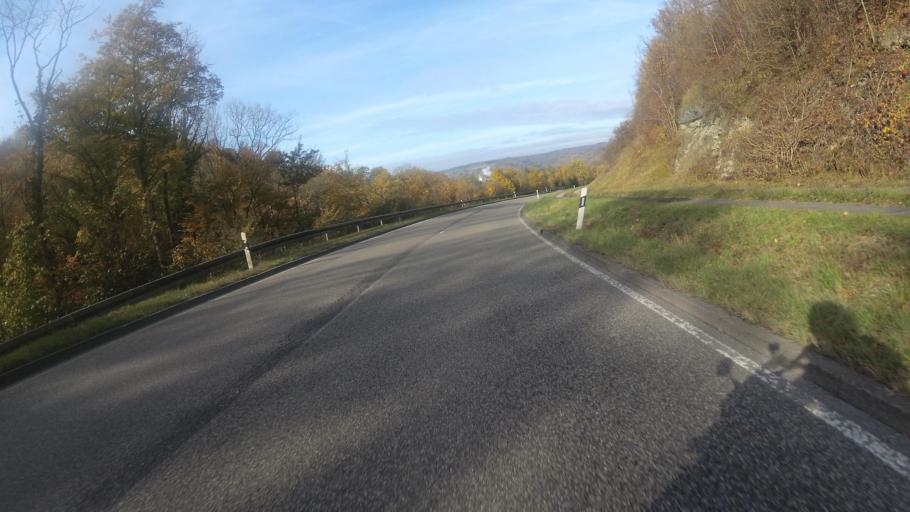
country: DE
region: Baden-Wuerttemberg
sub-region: Regierungsbezirk Stuttgart
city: Mockmuhl
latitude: 49.2896
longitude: 9.3320
